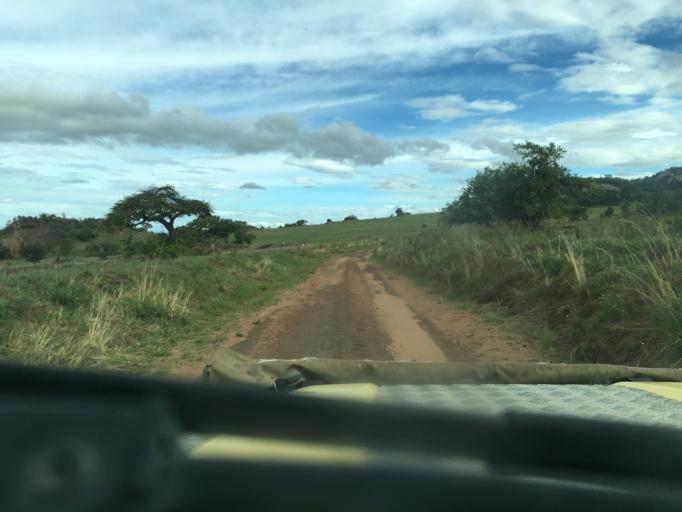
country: TZ
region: Mara
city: Mugumu
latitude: -1.9977
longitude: 35.1652
